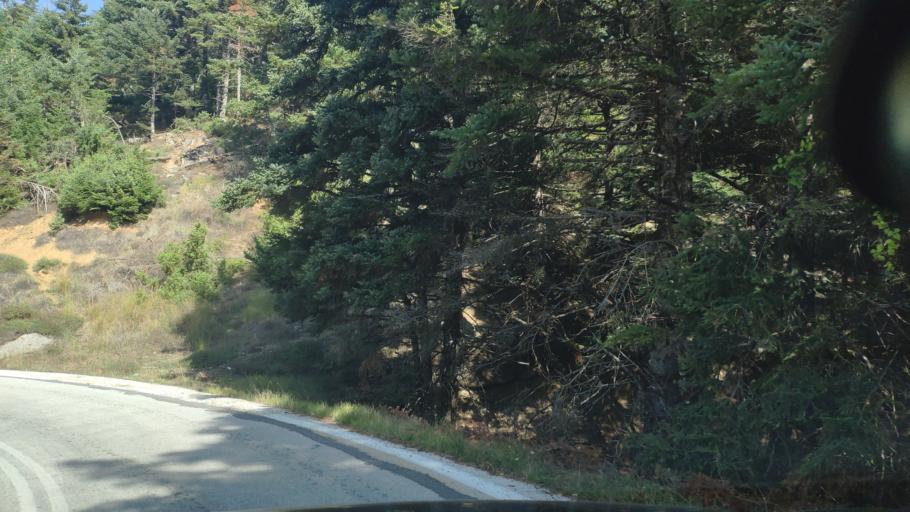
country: GR
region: West Greece
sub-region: Nomos Achaias
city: Aiyira
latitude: 37.8664
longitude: 22.3658
